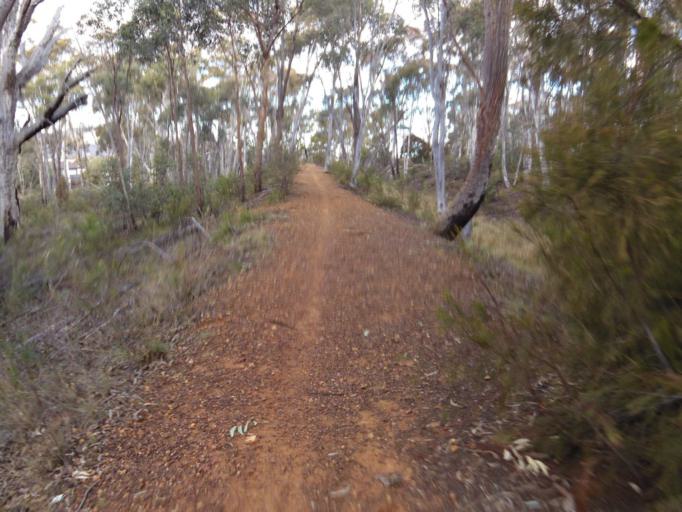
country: AU
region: Australian Capital Territory
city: Acton
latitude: -35.2615
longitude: 149.1108
